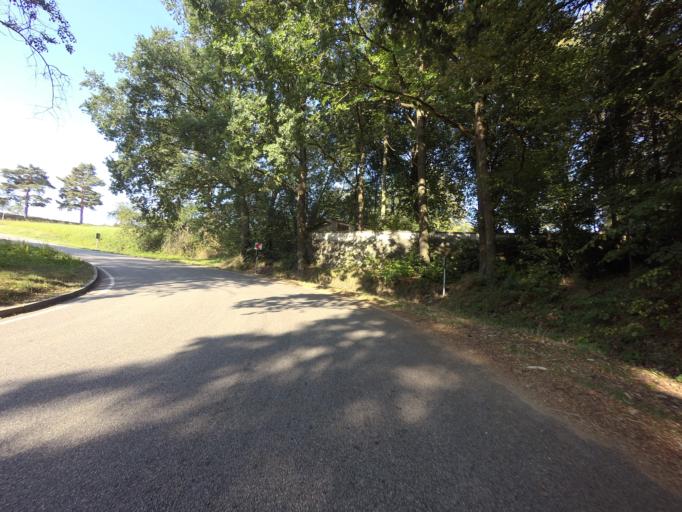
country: CZ
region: Jihocesky
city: Tyn nad Vltavou
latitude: 49.2552
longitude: 14.4189
